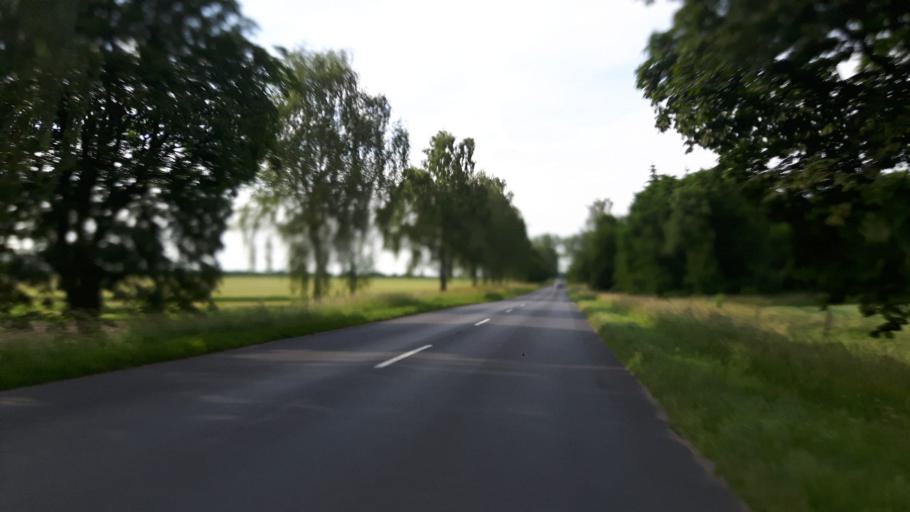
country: PL
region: West Pomeranian Voivodeship
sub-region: Powiat gryficki
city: Gryfice
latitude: 53.8917
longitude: 15.2074
